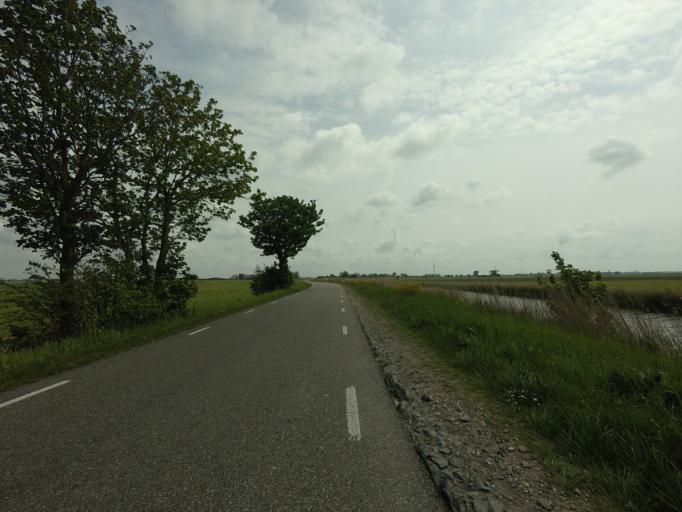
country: NL
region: Friesland
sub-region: Sudwest Fryslan
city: Bolsward
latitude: 53.1060
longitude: 5.5078
